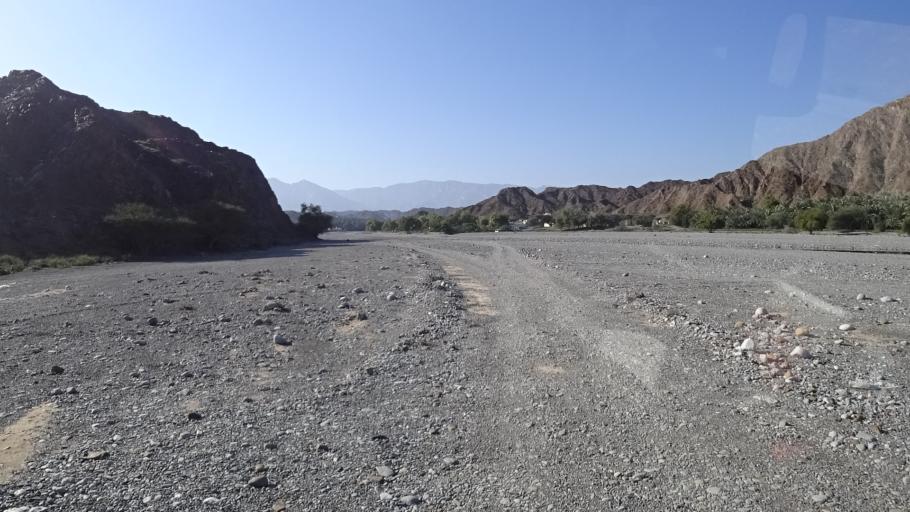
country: OM
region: Al Batinah
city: Bayt al `Awabi
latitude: 23.3977
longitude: 57.6636
